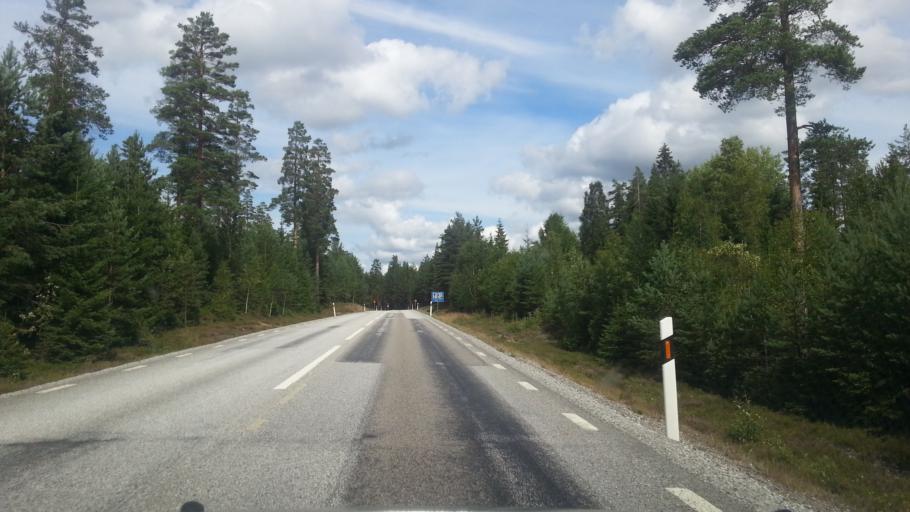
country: SE
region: Vaestmanland
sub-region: Skinnskattebergs Kommun
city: Skinnskatteberg
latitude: 59.7998
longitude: 15.5458
